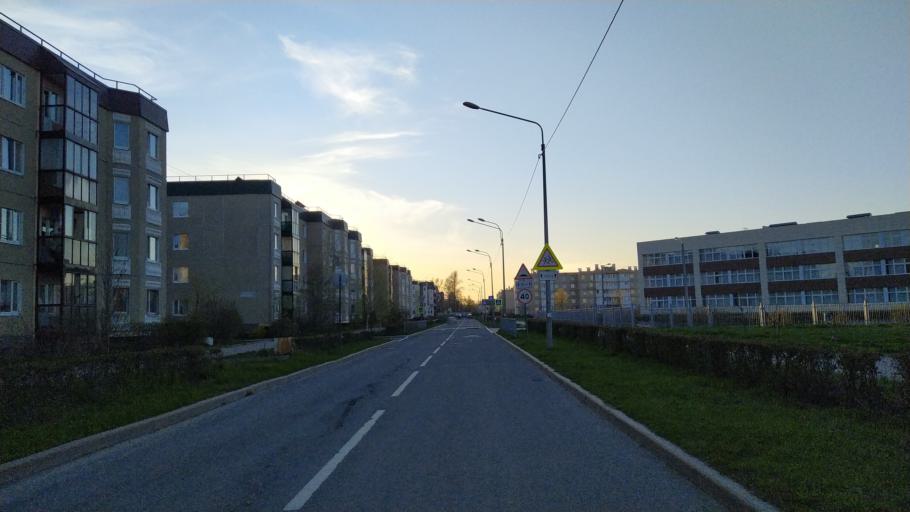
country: RU
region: St.-Petersburg
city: Pushkin
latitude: 59.7036
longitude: 30.3828
